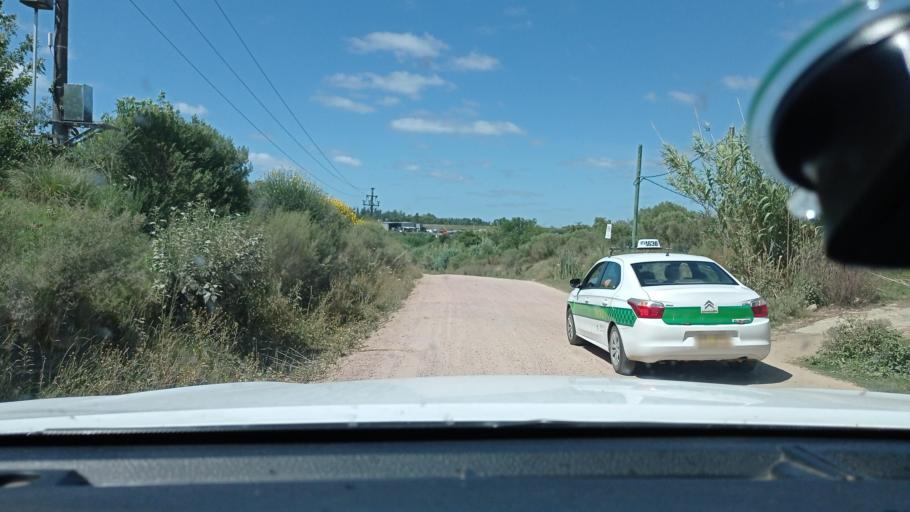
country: UY
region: Canelones
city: Pando
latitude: -34.7222
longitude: -55.9729
